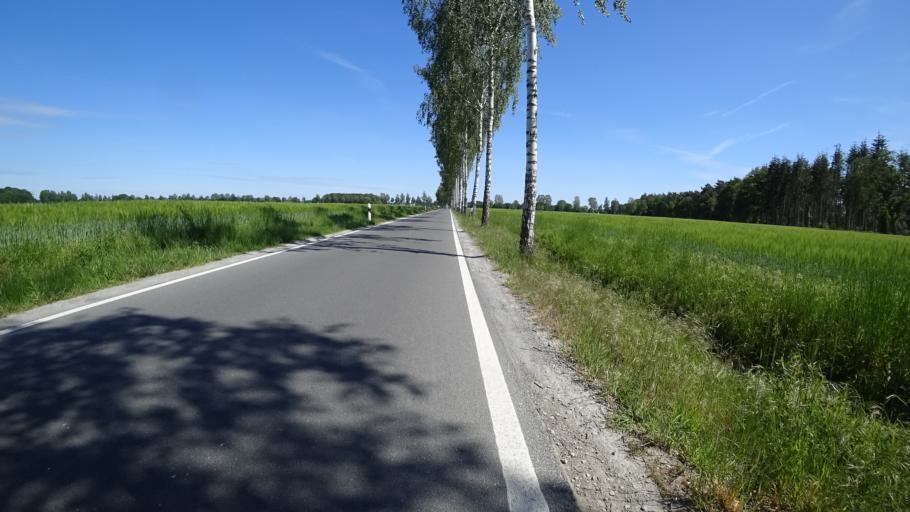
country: DE
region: North Rhine-Westphalia
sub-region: Regierungsbezirk Detmold
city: Rheda-Wiedenbruck
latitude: 51.8436
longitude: 8.3444
